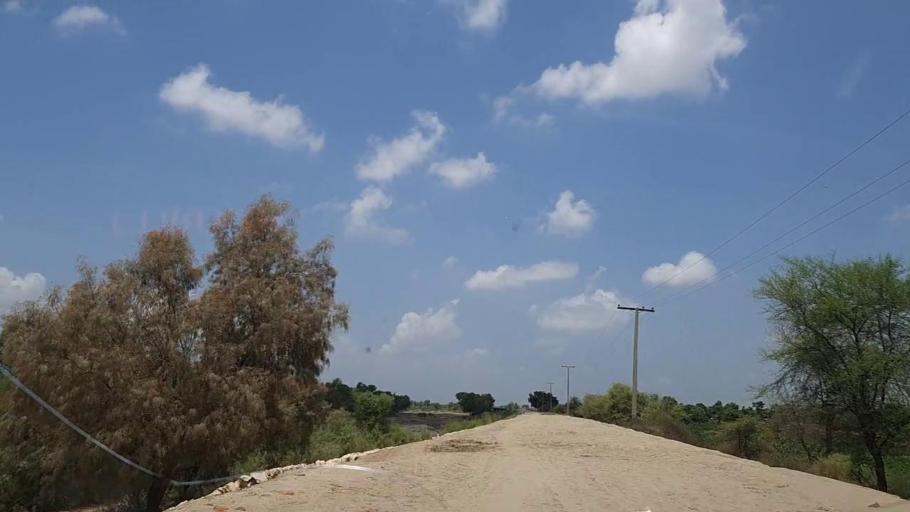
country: PK
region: Sindh
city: Tharu Shah
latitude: 26.9249
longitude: 67.9899
